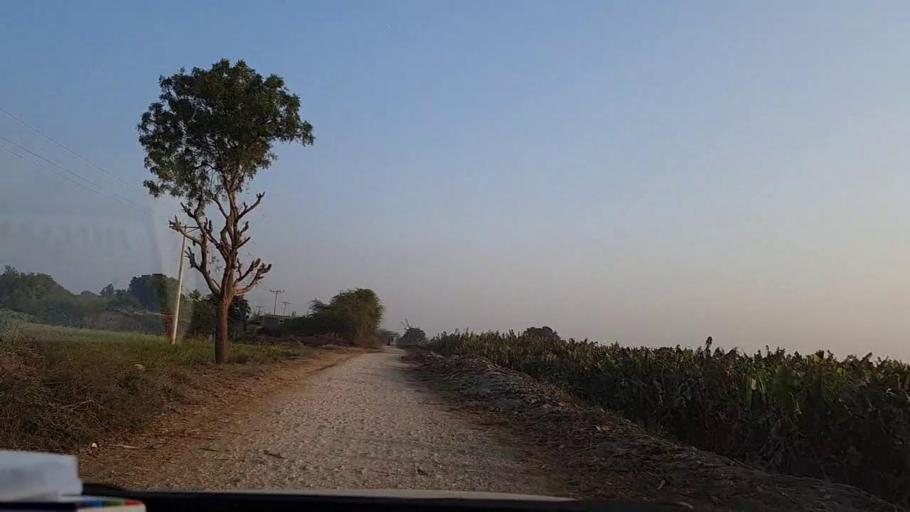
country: PK
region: Sindh
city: Tando Ghulam Ali
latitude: 25.1846
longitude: 68.9201
